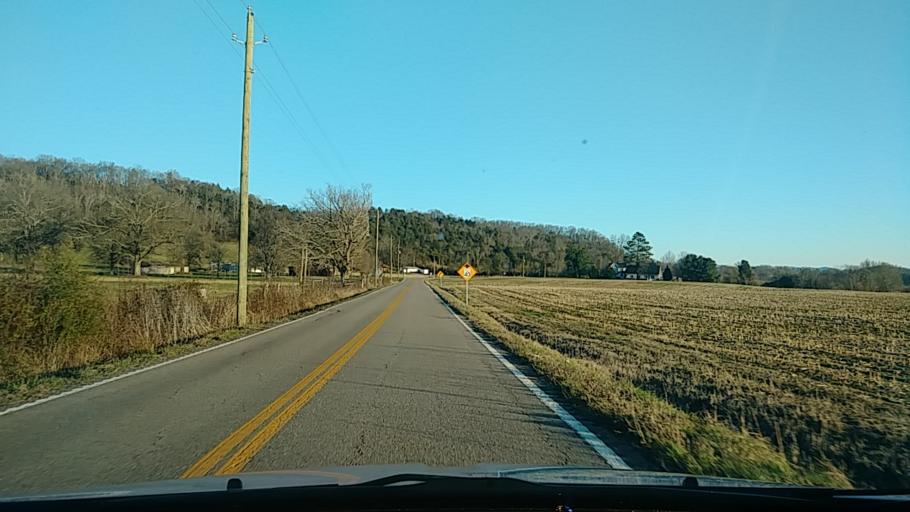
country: US
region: Tennessee
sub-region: Jefferson County
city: White Pine
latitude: 36.1320
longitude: -83.1308
